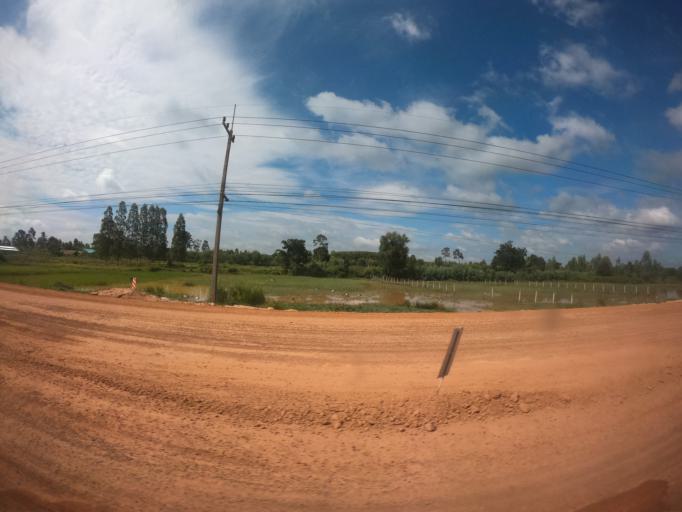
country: TH
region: Surin
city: Kap Choeng
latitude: 14.4611
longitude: 103.6570
